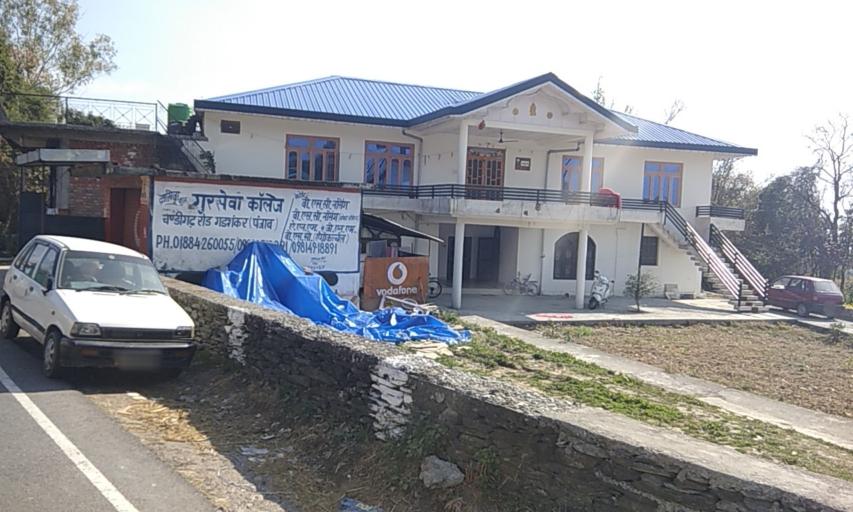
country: IN
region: Himachal Pradesh
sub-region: Kangra
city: Dharmsala
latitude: 32.1659
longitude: 76.3947
